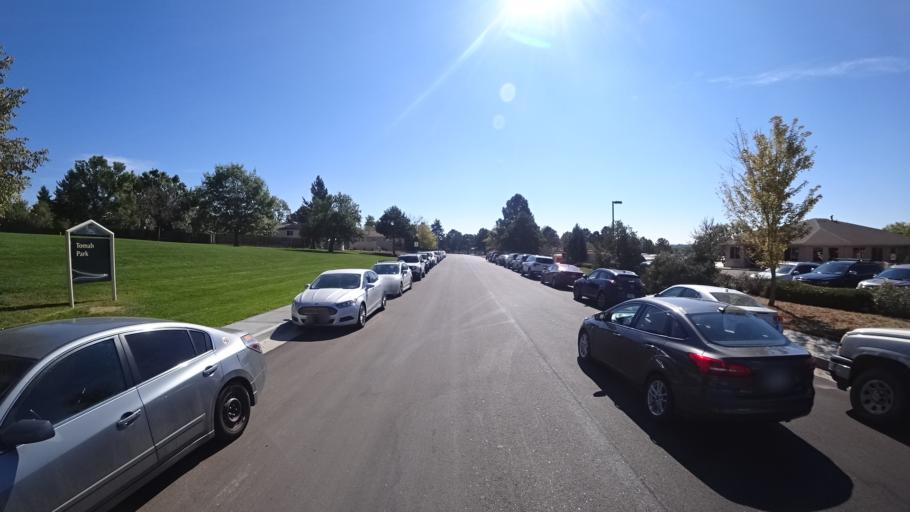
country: US
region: Colorado
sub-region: El Paso County
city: Colorado Springs
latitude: 38.9068
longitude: -104.7770
